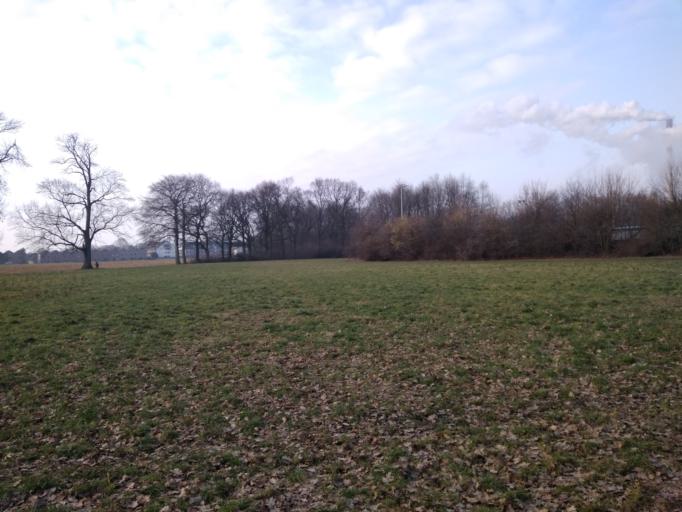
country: DE
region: North Rhine-Westphalia
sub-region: Regierungsbezirk Munster
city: Gladbeck
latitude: 51.5876
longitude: 7.0130
